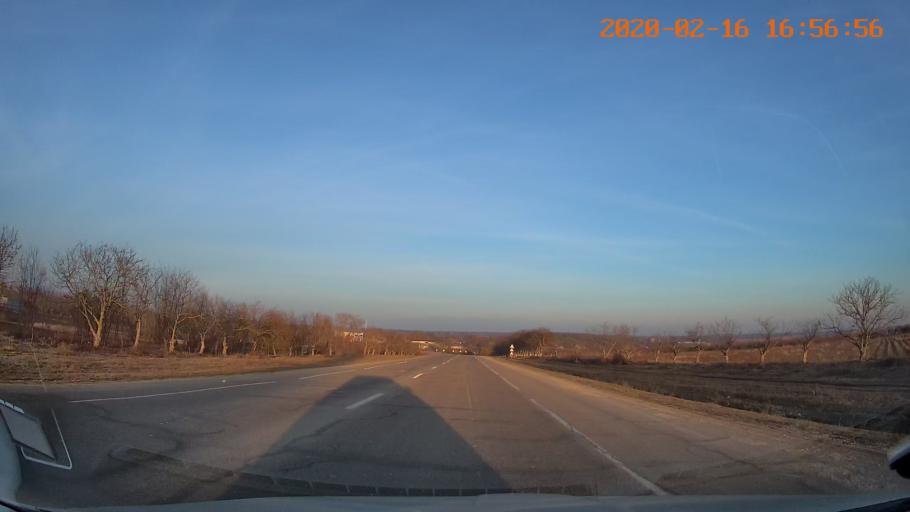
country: MD
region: Briceni
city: Briceni
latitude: 48.3374
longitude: 27.0597
